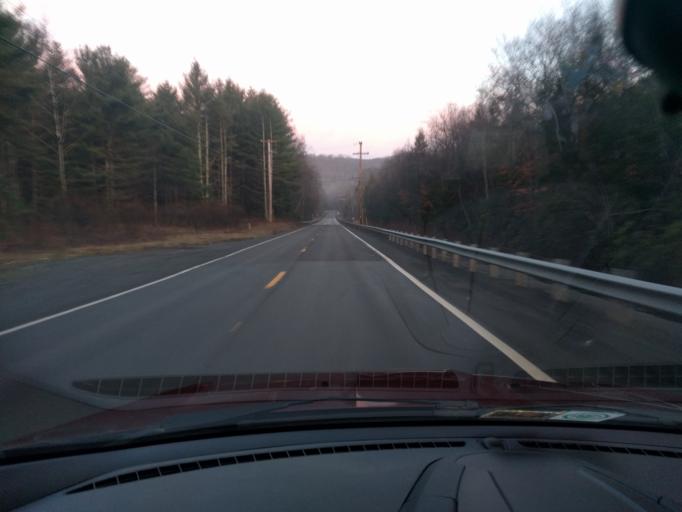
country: US
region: West Virginia
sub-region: Greenbrier County
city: Rainelle
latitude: 38.0461
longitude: -80.9252
